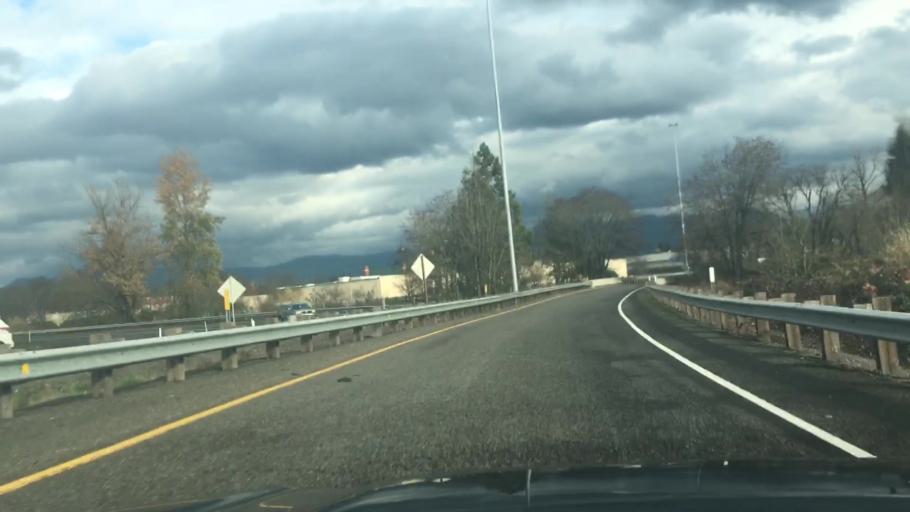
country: US
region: Oregon
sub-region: Lane County
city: Eugene
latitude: 44.0899
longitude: -123.0987
